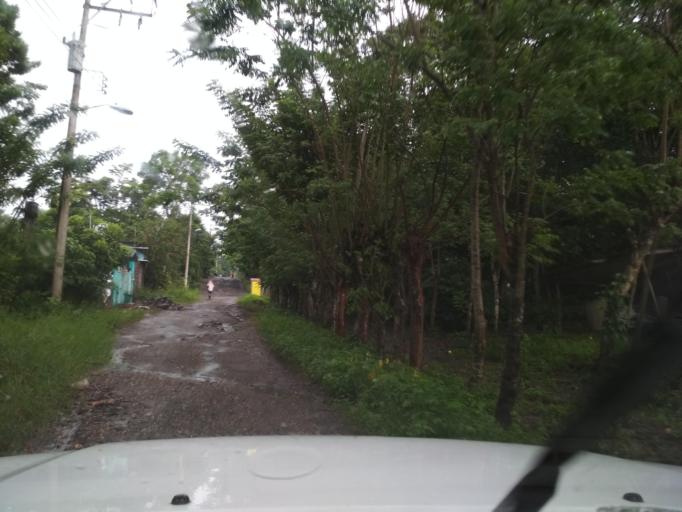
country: MX
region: Veracruz
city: Santiago Tuxtla
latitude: 18.4509
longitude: -95.3170
